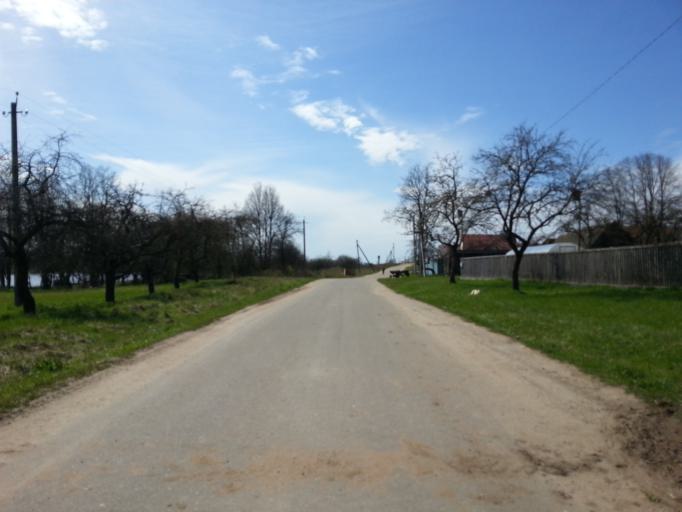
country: BY
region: Minsk
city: Khalopyenichy
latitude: 54.4368
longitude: 28.8834
